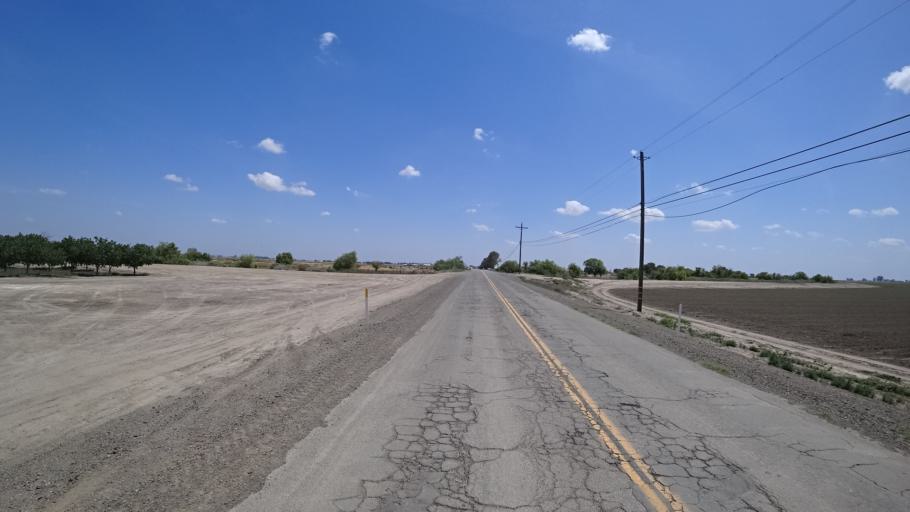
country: US
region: California
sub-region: Kings County
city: Stratford
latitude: 36.1895
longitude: -119.8473
